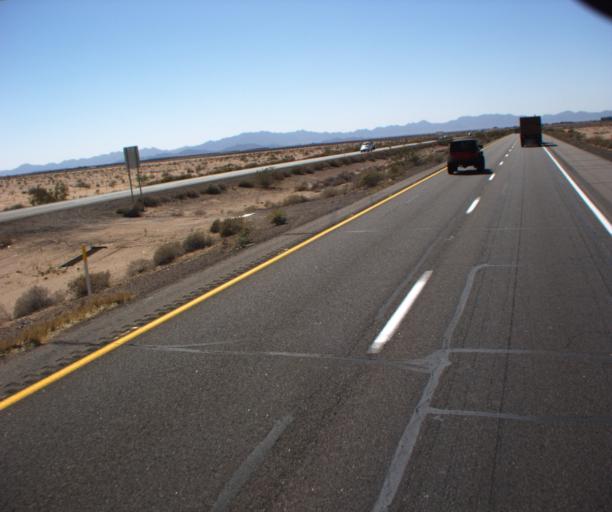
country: US
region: Arizona
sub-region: Yuma County
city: Wellton
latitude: 32.6860
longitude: -114.0016
